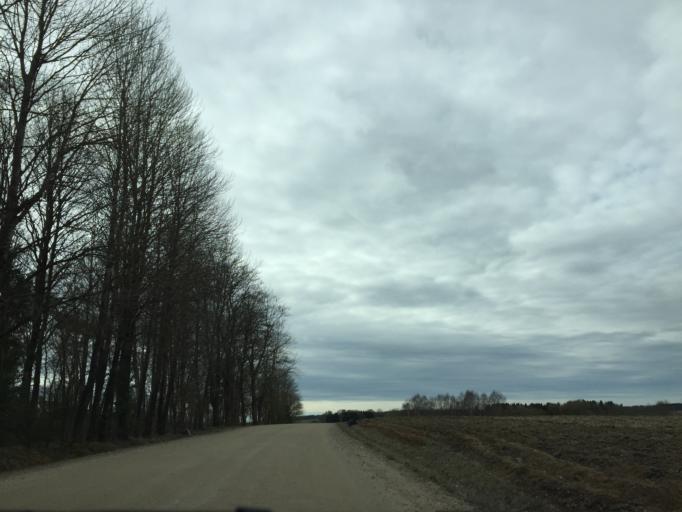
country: LT
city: Silale
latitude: 55.6187
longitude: 22.2008
